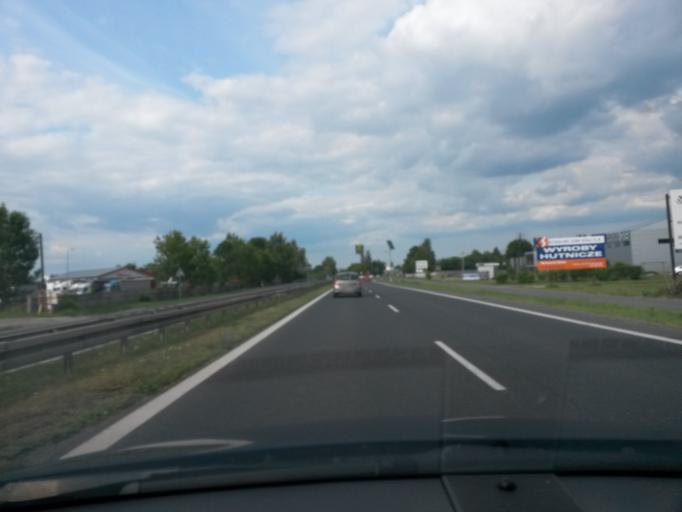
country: PL
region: Masovian Voivodeship
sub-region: Powiat pruszkowski
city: Nadarzyn
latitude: 52.0792
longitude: 20.7873
